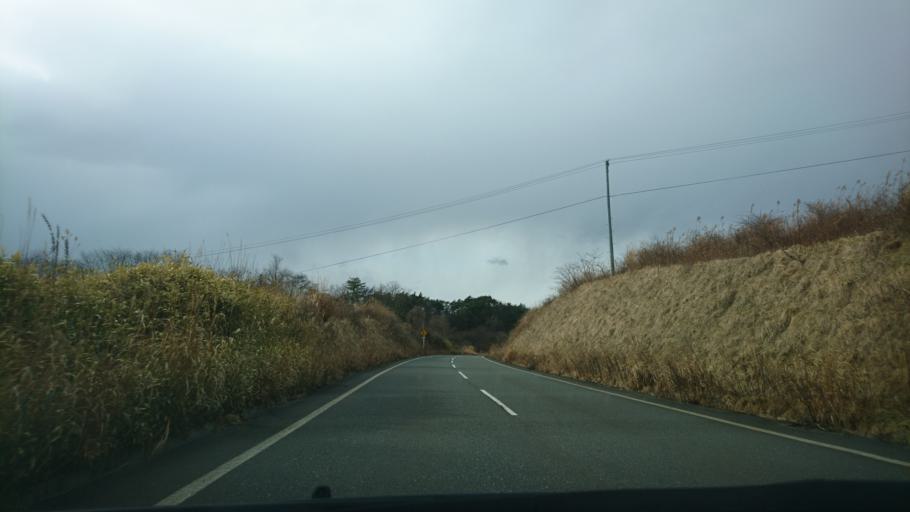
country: JP
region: Iwate
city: Ichinoseki
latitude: 38.8419
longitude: 141.2128
